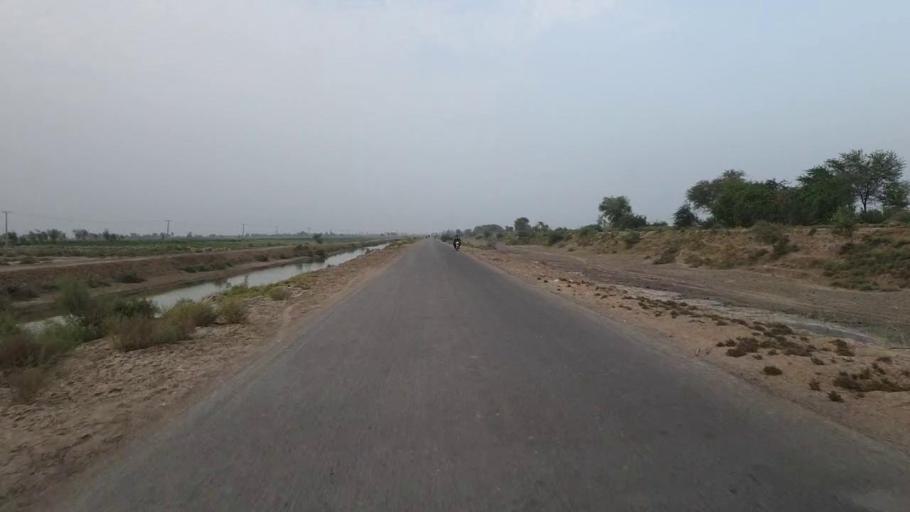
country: PK
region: Sindh
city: Daur
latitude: 26.4410
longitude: 68.2775
